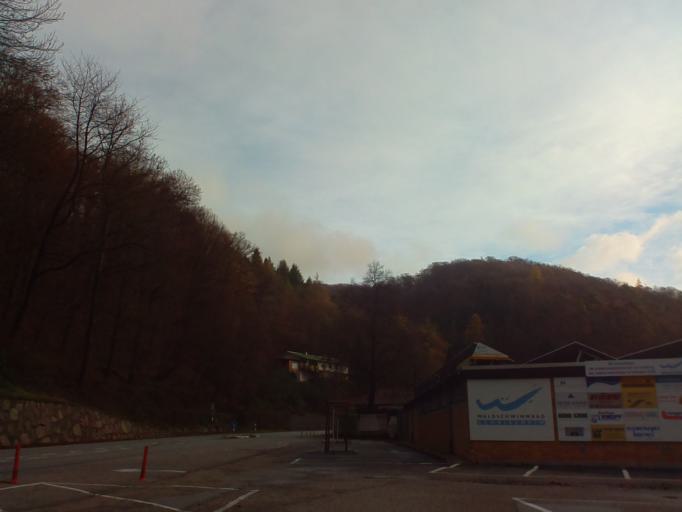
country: DE
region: Baden-Wuerttemberg
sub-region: Karlsruhe Region
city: Dossenheim
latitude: 49.4761
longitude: 8.7046
